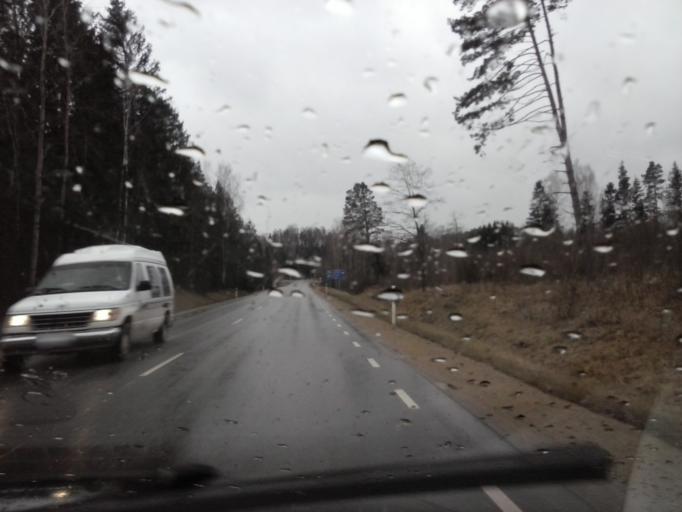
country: EE
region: Polvamaa
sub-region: Polva linn
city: Polva
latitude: 58.0462
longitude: 27.0736
